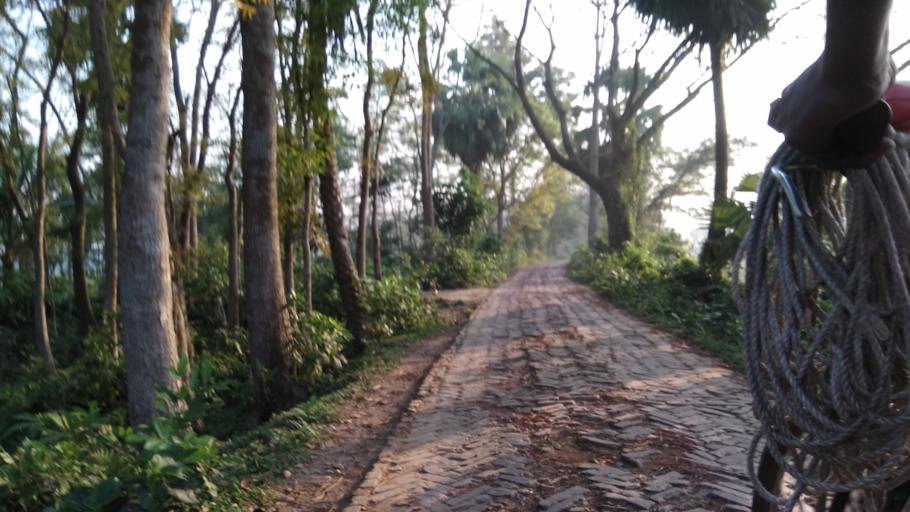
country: BD
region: Barisal
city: Mehendiganj
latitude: 22.9329
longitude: 90.4136
